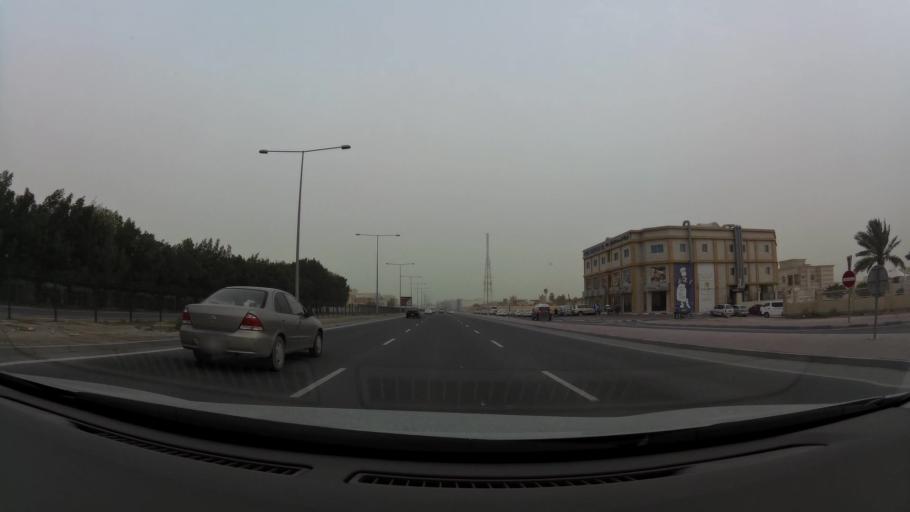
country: QA
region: Baladiyat ad Dawhah
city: Doha
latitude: 25.2341
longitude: 51.4839
